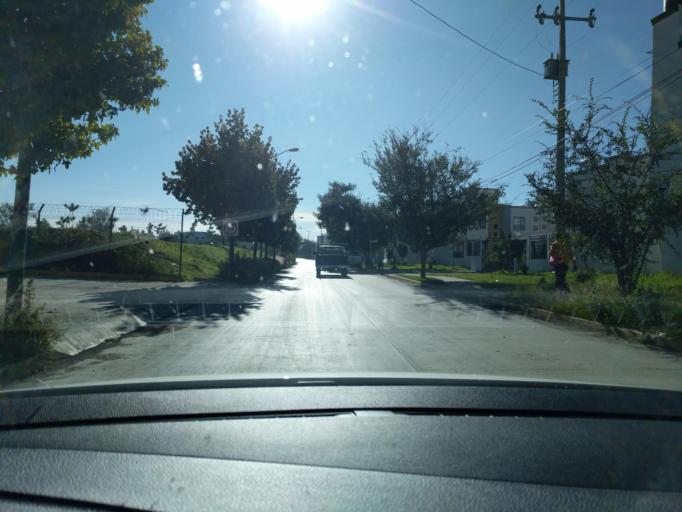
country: MX
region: Puebla
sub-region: Huejotzingo
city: Los Encinos
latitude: 19.1761
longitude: -98.3894
